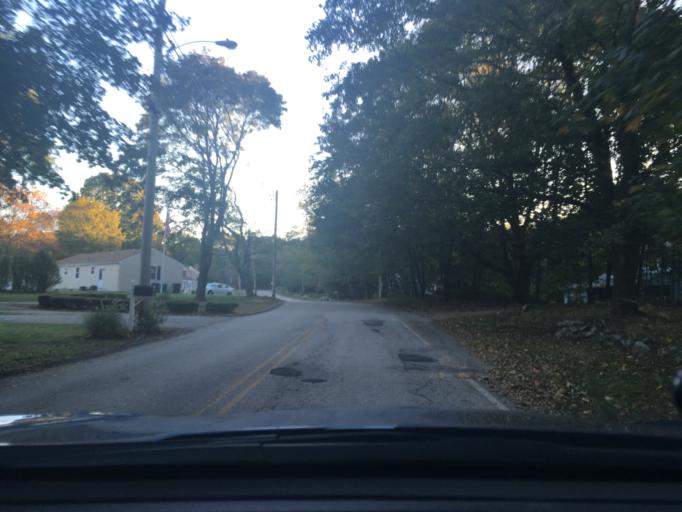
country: US
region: Rhode Island
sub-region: Kent County
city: East Greenwich
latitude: 41.6367
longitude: -71.4566
